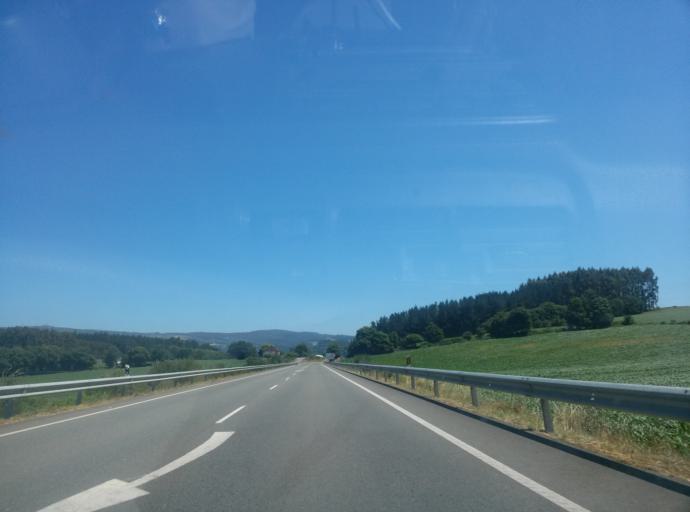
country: ES
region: Galicia
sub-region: Provincia de Lugo
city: Meira
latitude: 43.2295
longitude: -7.3344
